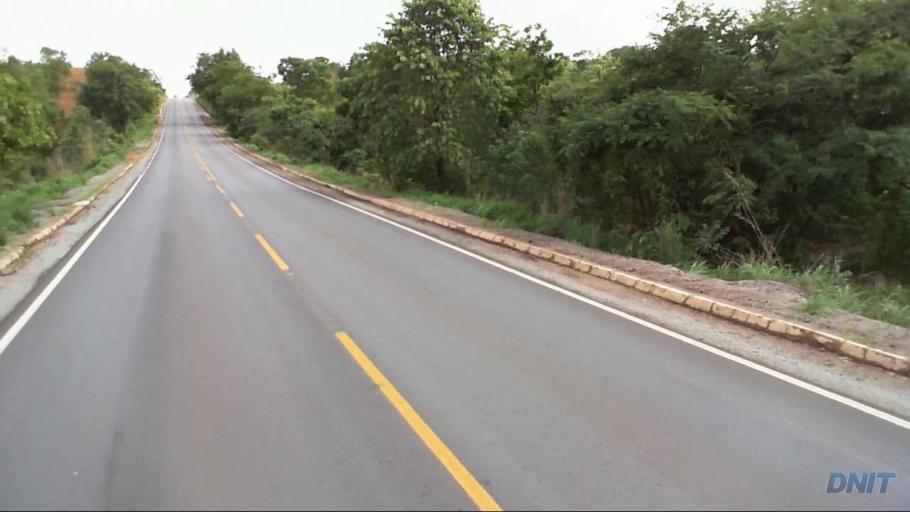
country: BR
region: Goias
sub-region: Padre Bernardo
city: Padre Bernardo
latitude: -15.2140
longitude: -48.2813
